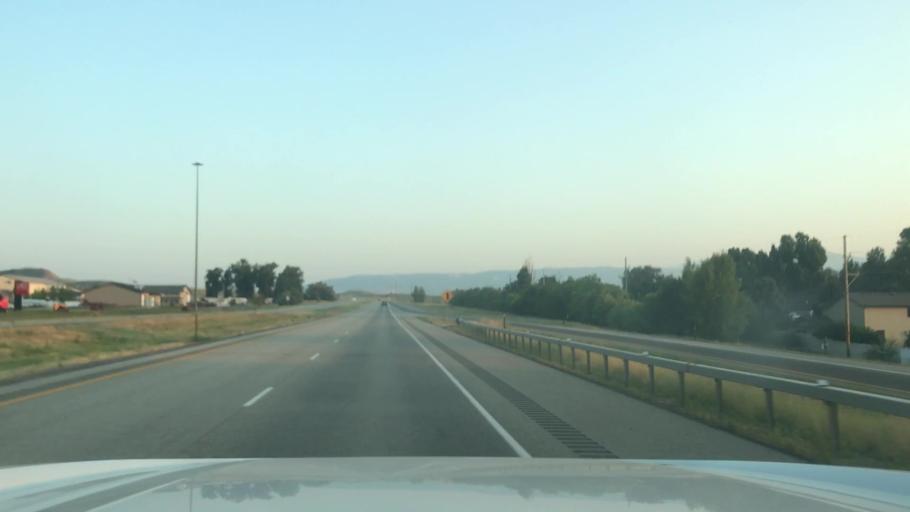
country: US
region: Wyoming
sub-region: Sheridan County
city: Sheridan
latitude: 44.7717
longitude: -106.9369
